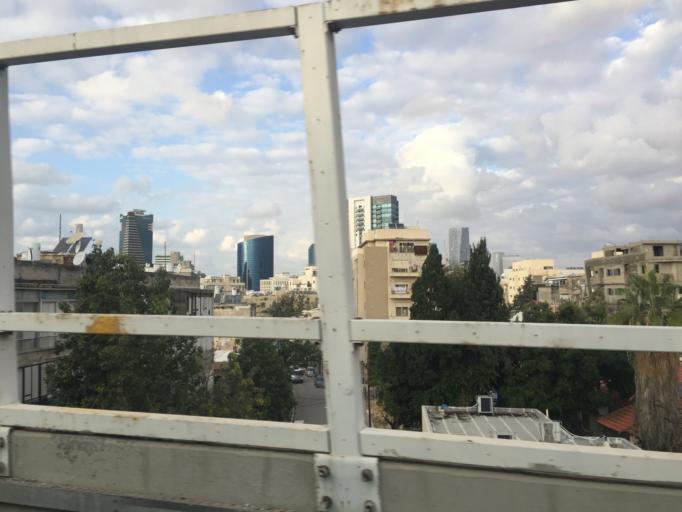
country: IL
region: Tel Aviv
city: Tel Aviv
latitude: 32.0561
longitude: 34.7813
